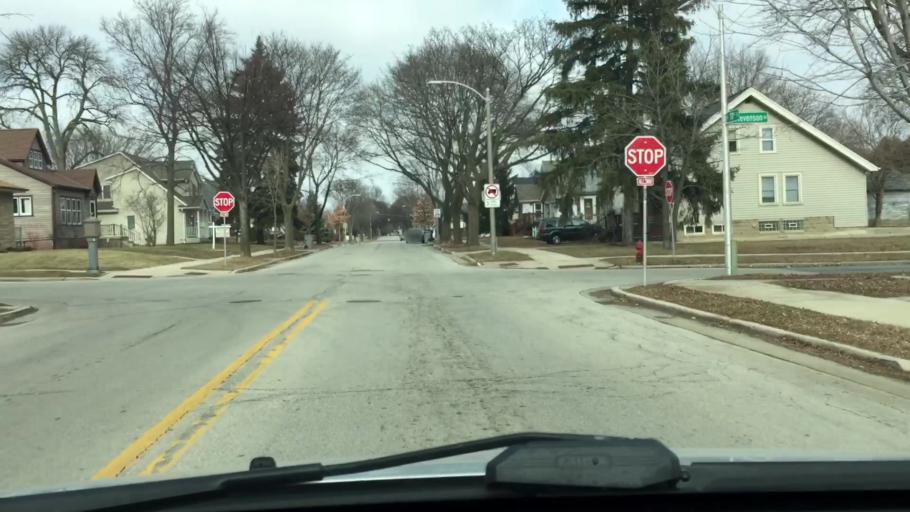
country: US
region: Wisconsin
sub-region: Milwaukee County
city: West Allis
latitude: 43.0319
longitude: -87.9998
